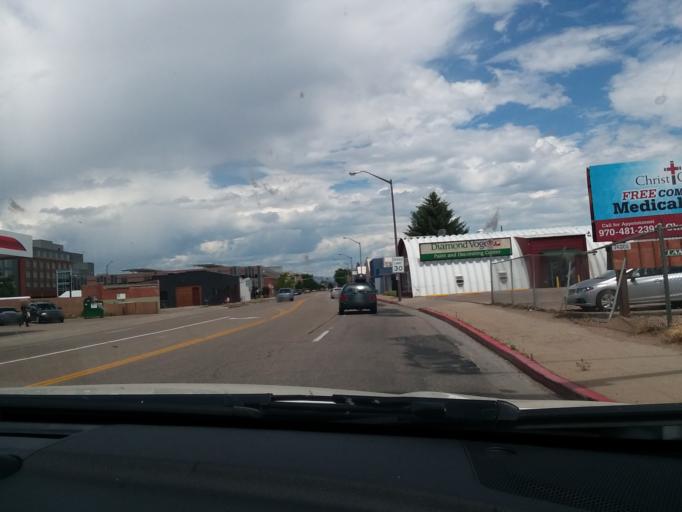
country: US
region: Colorado
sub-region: Larimer County
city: Fort Collins
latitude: 40.5873
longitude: -105.0716
